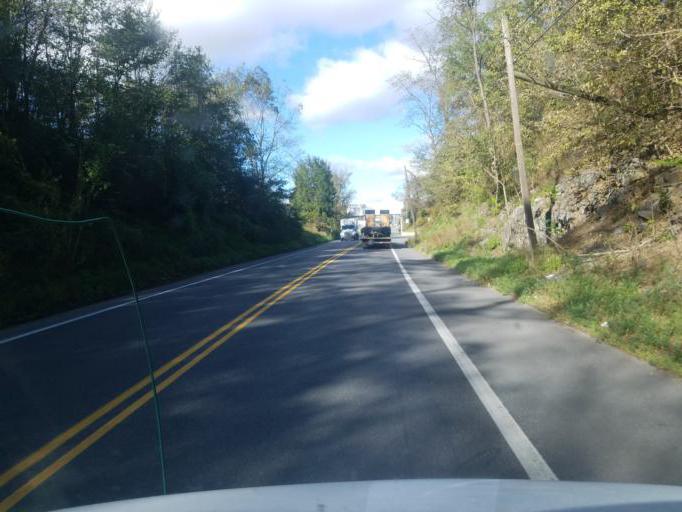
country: US
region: Pennsylvania
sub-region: Franklin County
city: Waynesboro
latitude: 39.7712
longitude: -77.6493
